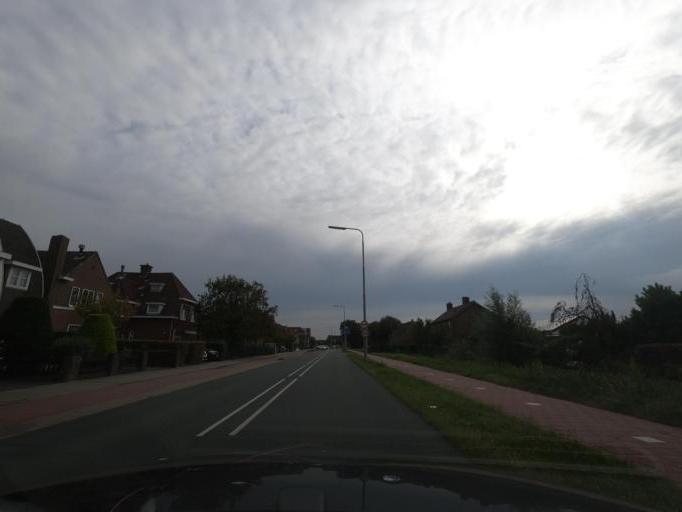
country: NL
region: South Holland
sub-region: Gemeente Westland
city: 's-Gravenzande
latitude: 52.0097
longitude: 4.1614
